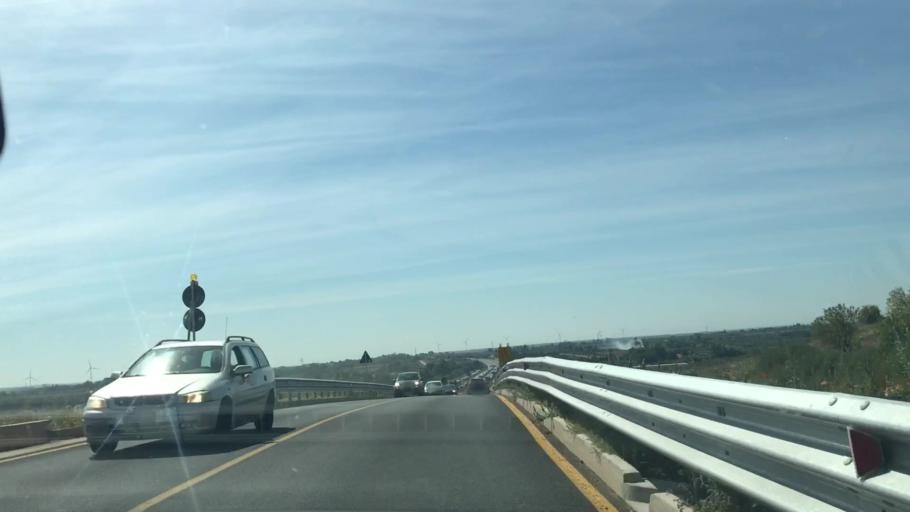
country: IT
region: Apulia
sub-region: Provincia di Bari
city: Altamura
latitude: 40.8087
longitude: 16.5557
